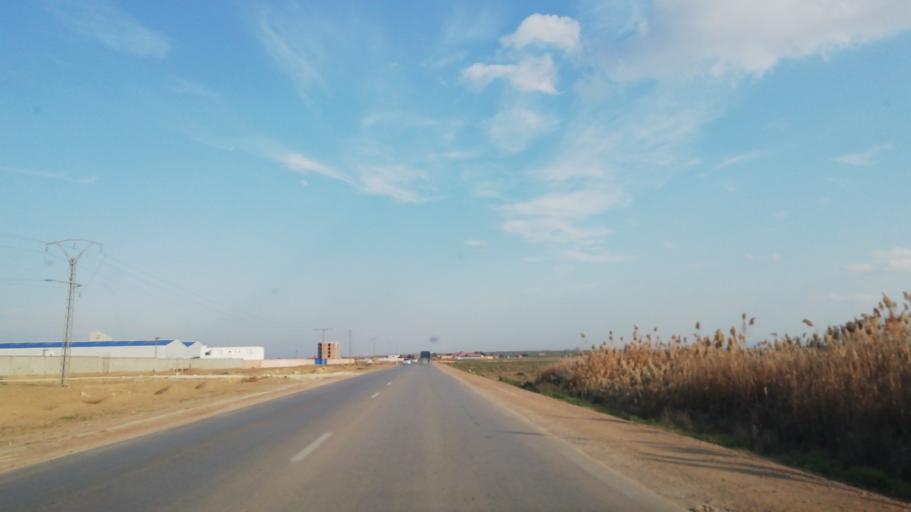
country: DZ
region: Relizane
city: Relizane
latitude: 35.8979
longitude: 0.5765
